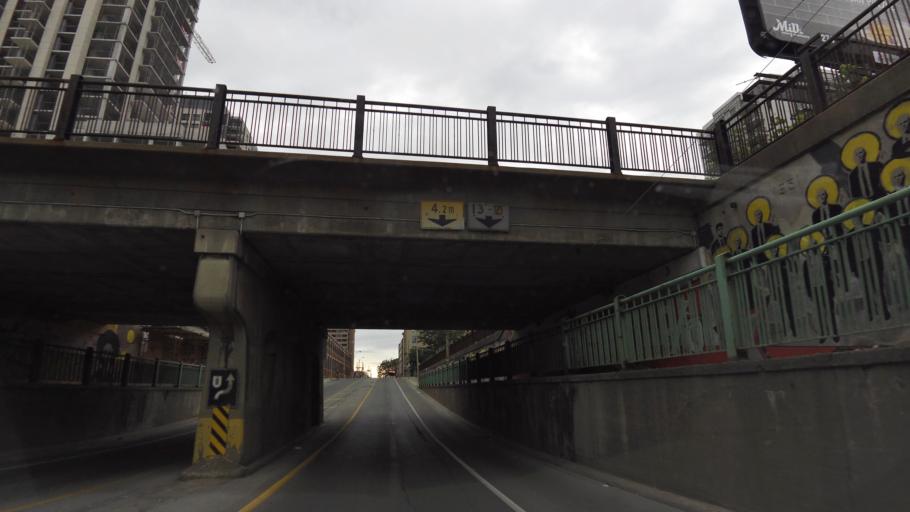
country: CA
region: Ontario
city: Toronto
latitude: 43.6662
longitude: -79.4489
